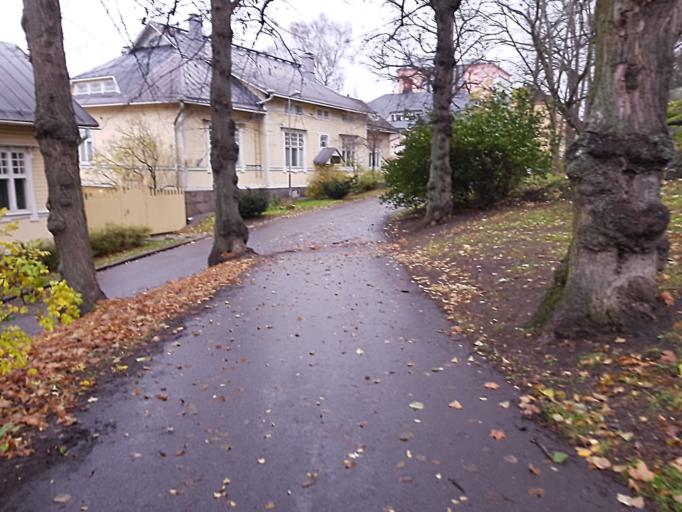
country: FI
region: Varsinais-Suomi
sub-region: Turku
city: Turku
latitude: 60.4541
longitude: 22.2606
